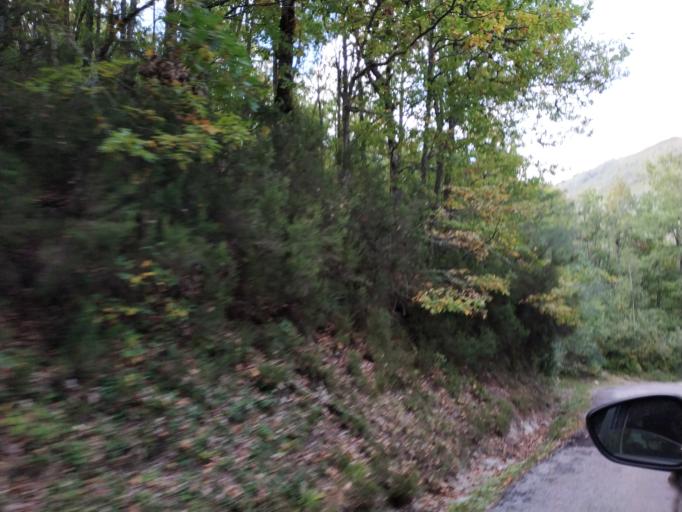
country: ES
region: Castille and Leon
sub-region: Provincia de Leon
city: Candin
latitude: 42.8654
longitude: -6.8617
